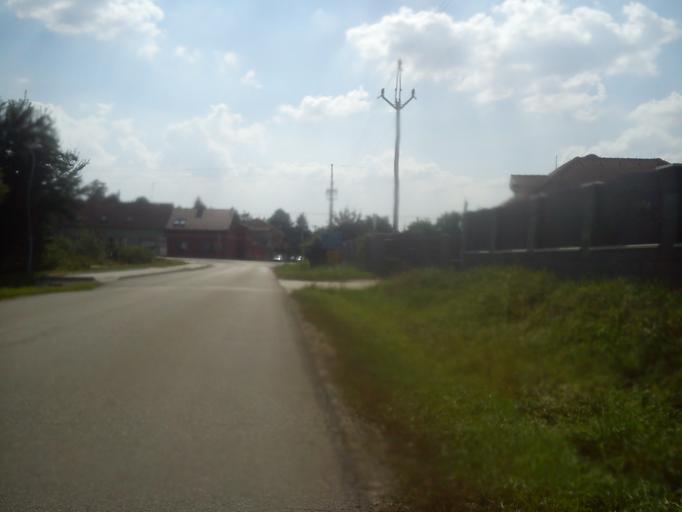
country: CZ
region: South Moravian
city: Sokolnice
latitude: 49.1135
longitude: 16.7280
